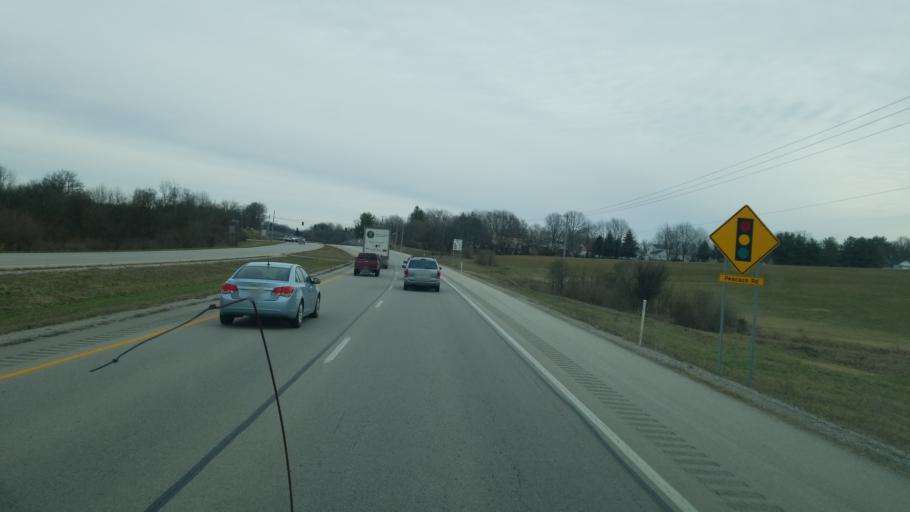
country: US
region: Kentucky
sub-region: Bourbon County
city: Paris
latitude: 38.2253
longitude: -84.2601
